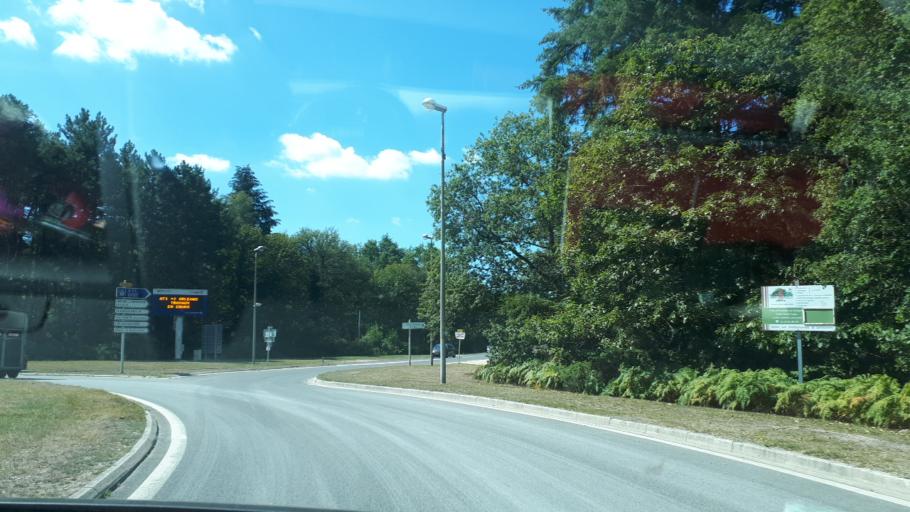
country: FR
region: Centre
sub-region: Departement du Loir-et-Cher
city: Lamotte-Beuvron
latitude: 47.5945
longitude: 2.0156
